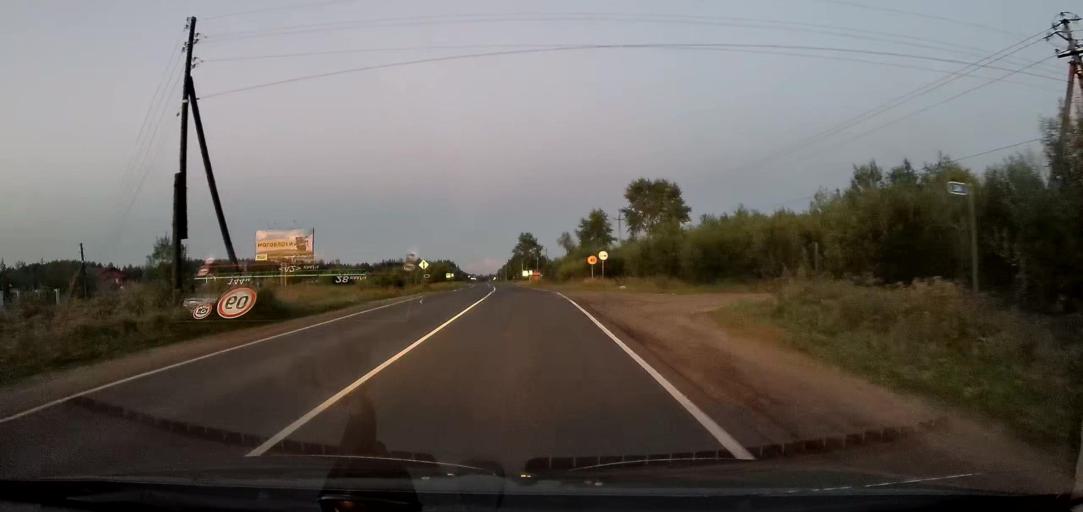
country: RU
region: Arkhangelskaya
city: Uyemskiy
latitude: 64.4473
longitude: 40.9468
